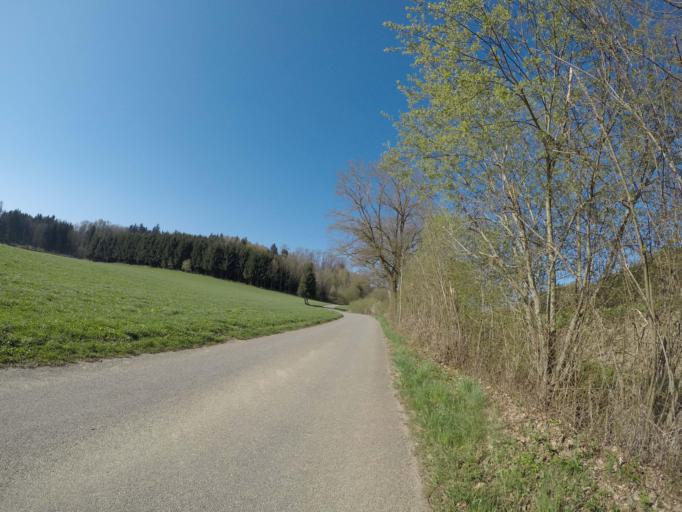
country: DE
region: Baden-Wuerttemberg
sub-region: Tuebingen Region
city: Ebenweiler
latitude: 47.8789
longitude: 9.5132
